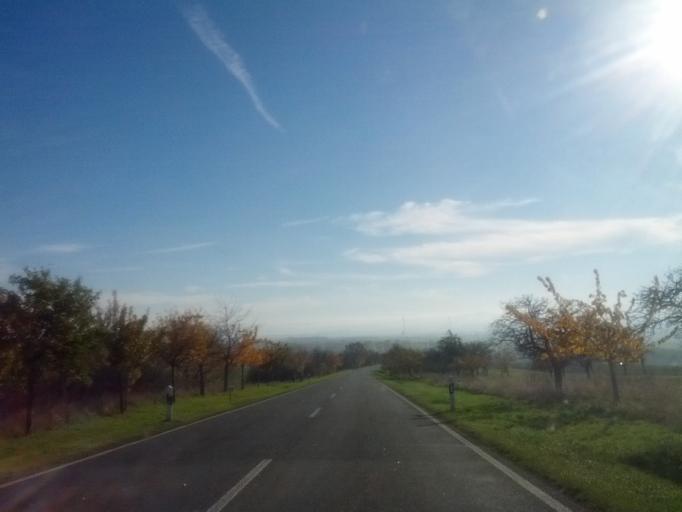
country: DE
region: Thuringia
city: Mechterstadt
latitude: 50.9540
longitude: 10.5575
